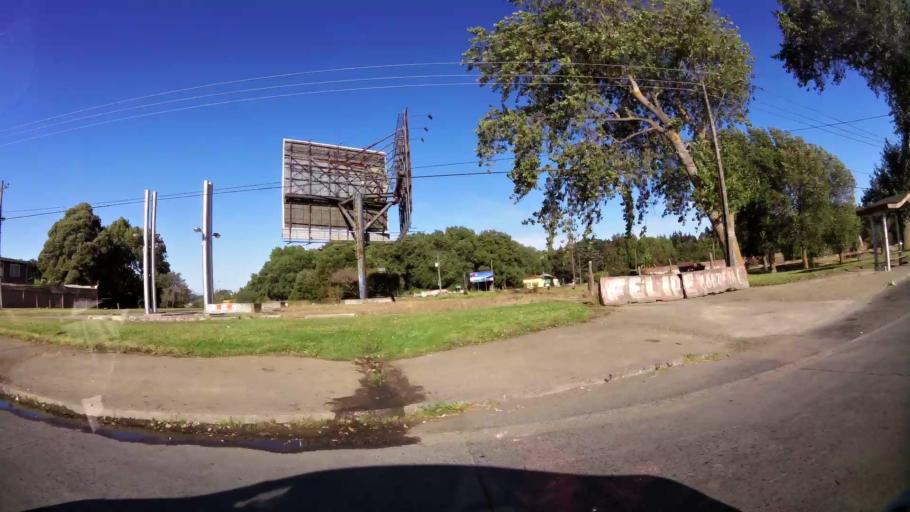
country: CL
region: Biobio
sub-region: Provincia de Concepcion
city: Concepcion
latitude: -36.8316
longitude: -73.1007
